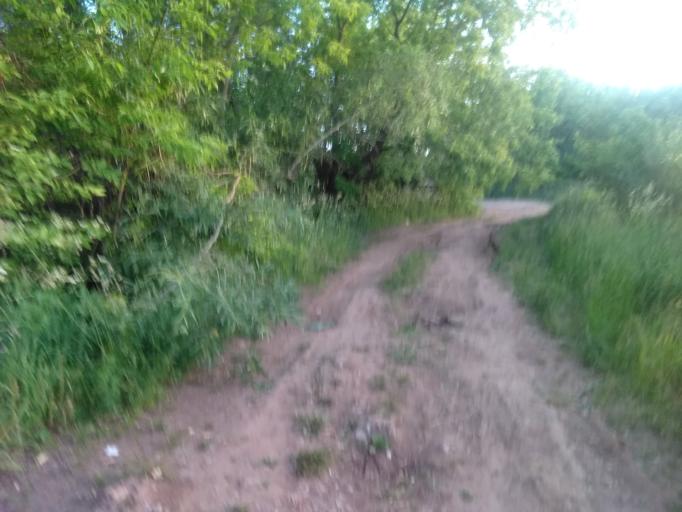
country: RU
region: Udmurtiya
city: Khokhryaki
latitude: 56.8547
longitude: 53.4054
